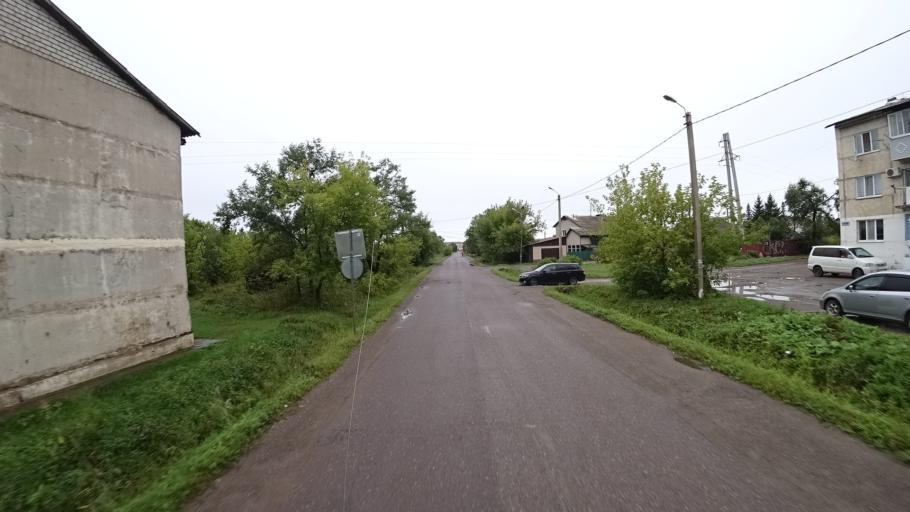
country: RU
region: Primorskiy
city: Monastyrishche
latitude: 44.2034
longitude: 132.4573
